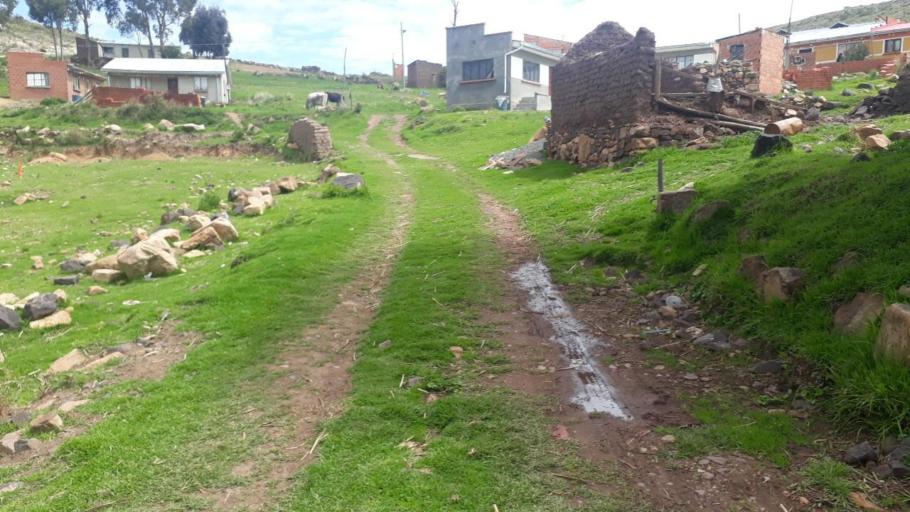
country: BO
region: La Paz
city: Batallas
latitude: -16.3450
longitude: -68.6367
